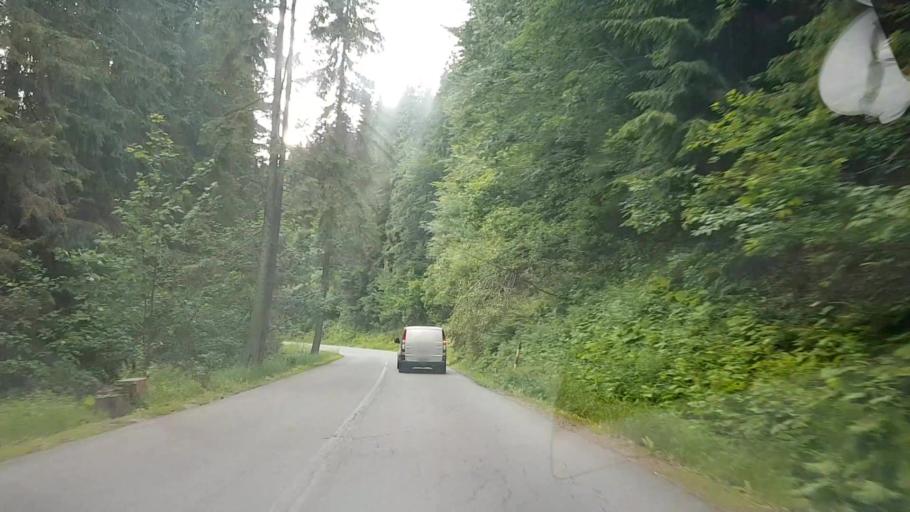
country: RO
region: Harghita
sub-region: Comuna Varsag
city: Varsag
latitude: 46.6726
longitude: 25.3272
